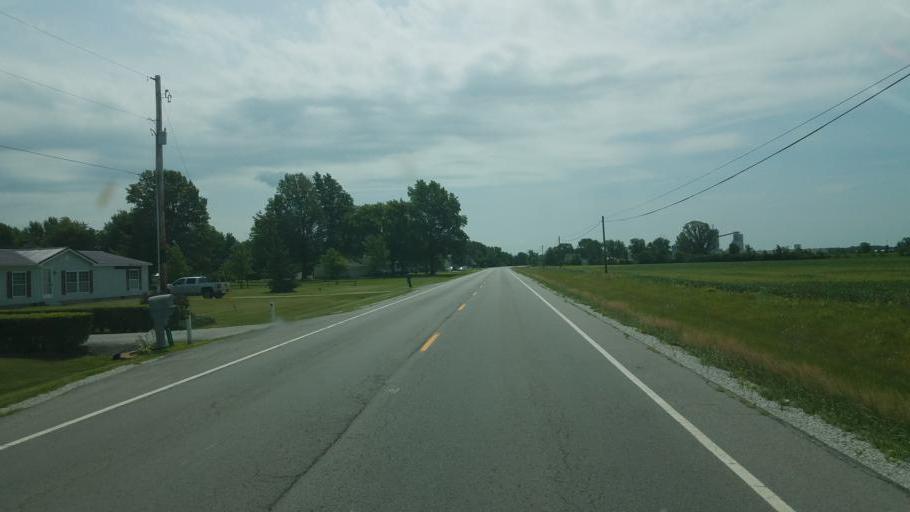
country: US
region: Ohio
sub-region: Wyandot County
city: Carey
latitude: 40.9180
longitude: -83.3444
